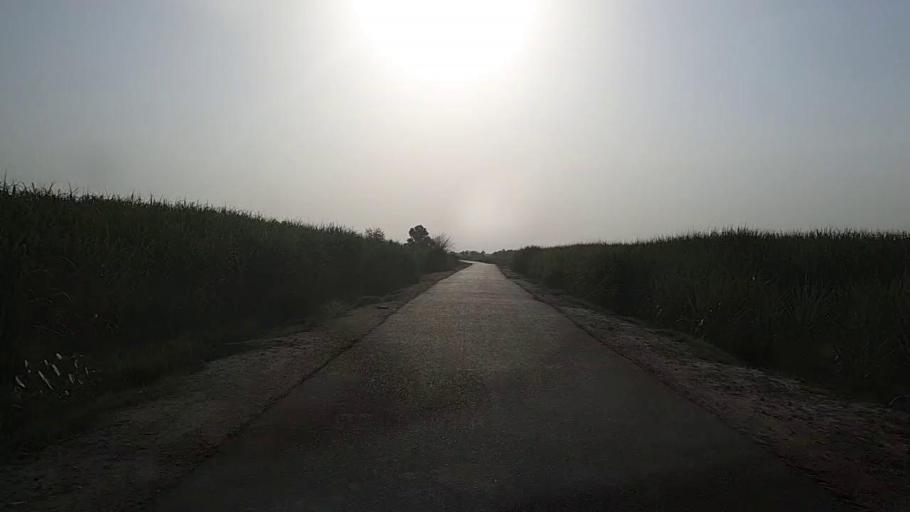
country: PK
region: Sindh
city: Ubauro
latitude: 28.1000
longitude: 69.8217
